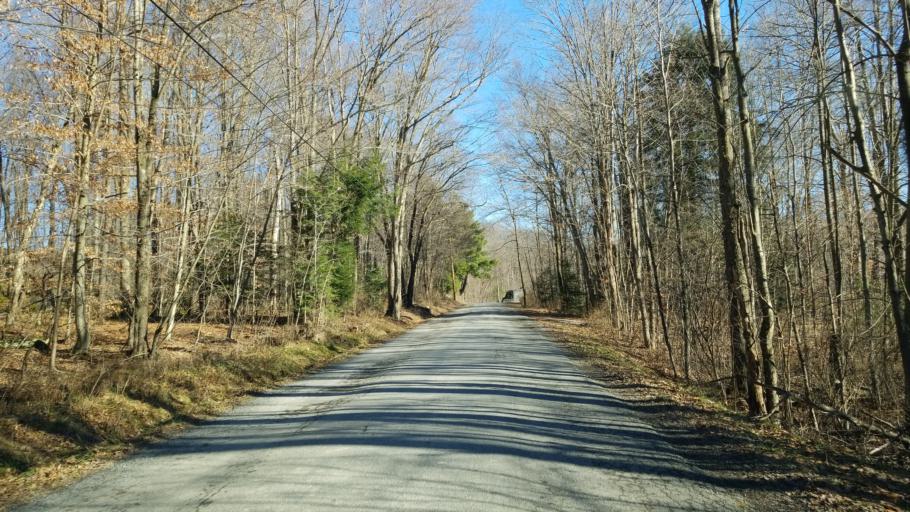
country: US
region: Pennsylvania
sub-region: Jefferson County
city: Falls Creek
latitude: 41.1596
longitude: -78.8400
